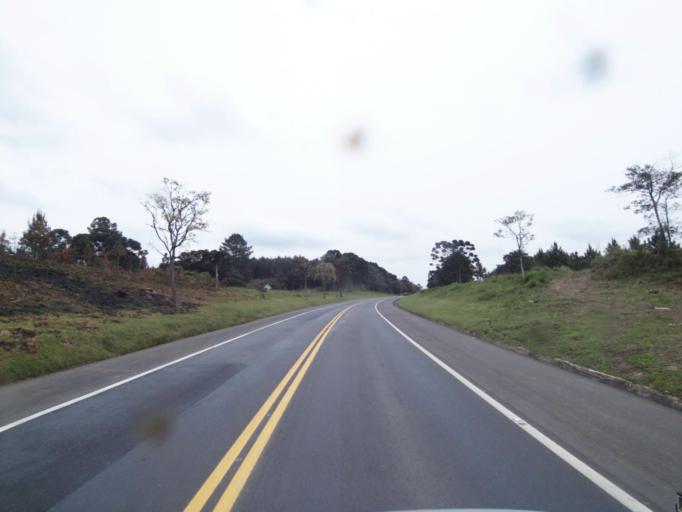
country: BR
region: Parana
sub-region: Irati
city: Irati
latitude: -25.4663
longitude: -50.5351
